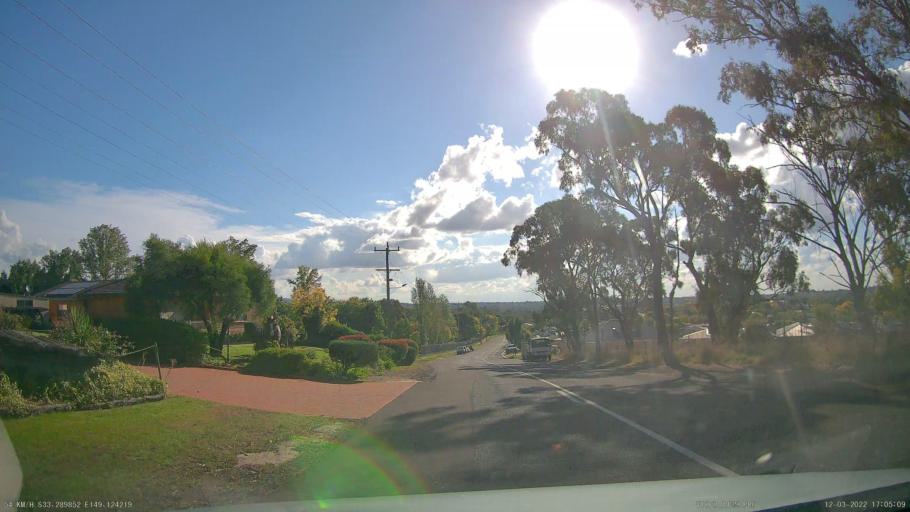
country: AU
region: New South Wales
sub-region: Orange Municipality
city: Orange
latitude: -33.2898
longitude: 149.1241
